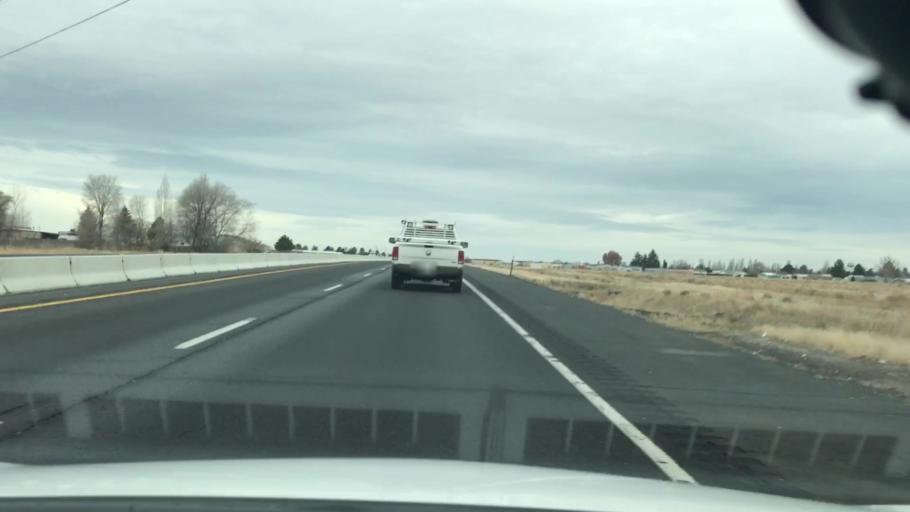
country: US
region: Washington
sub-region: Grant County
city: Cascade Valley
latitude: 47.1532
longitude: -119.3028
